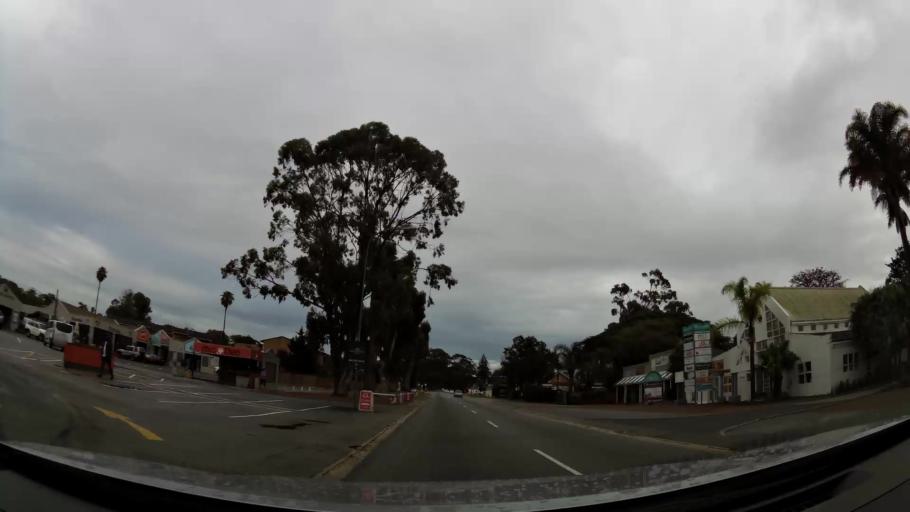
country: ZA
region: Eastern Cape
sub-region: Nelson Mandela Bay Metropolitan Municipality
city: Port Elizabeth
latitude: -33.9799
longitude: 25.5813
